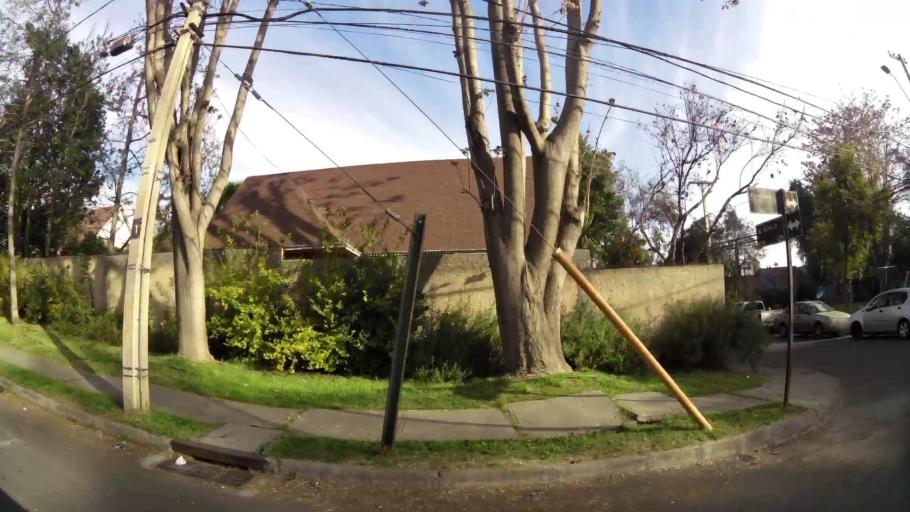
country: CL
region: Santiago Metropolitan
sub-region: Provincia de Santiago
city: Villa Presidente Frei, Nunoa, Santiago, Chile
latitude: -33.5076
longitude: -70.5584
